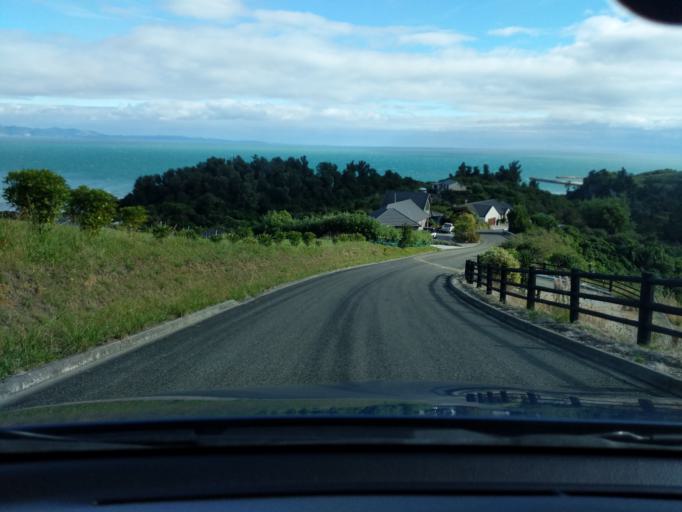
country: NZ
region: Tasman
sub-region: Tasman District
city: Takaka
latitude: -40.8373
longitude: 172.8903
